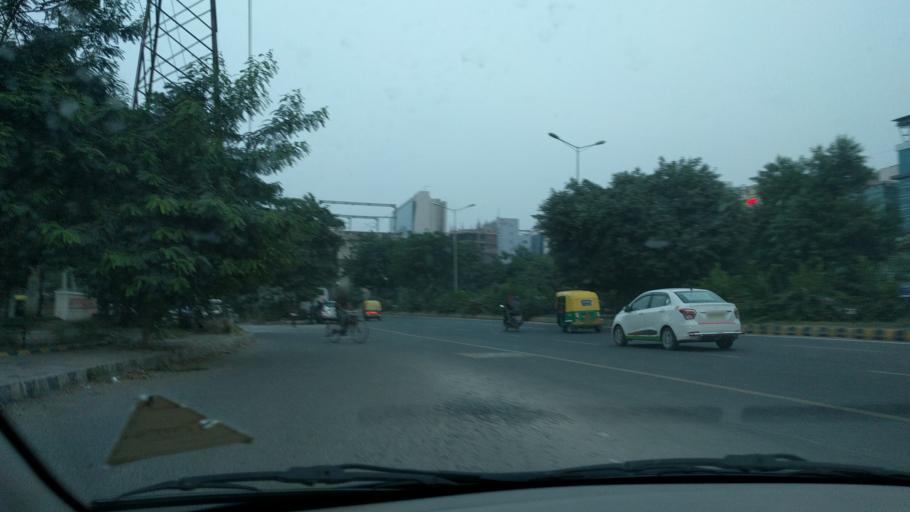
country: IN
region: Haryana
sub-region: Gurgaon
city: Gurgaon
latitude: 28.4535
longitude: 77.0673
